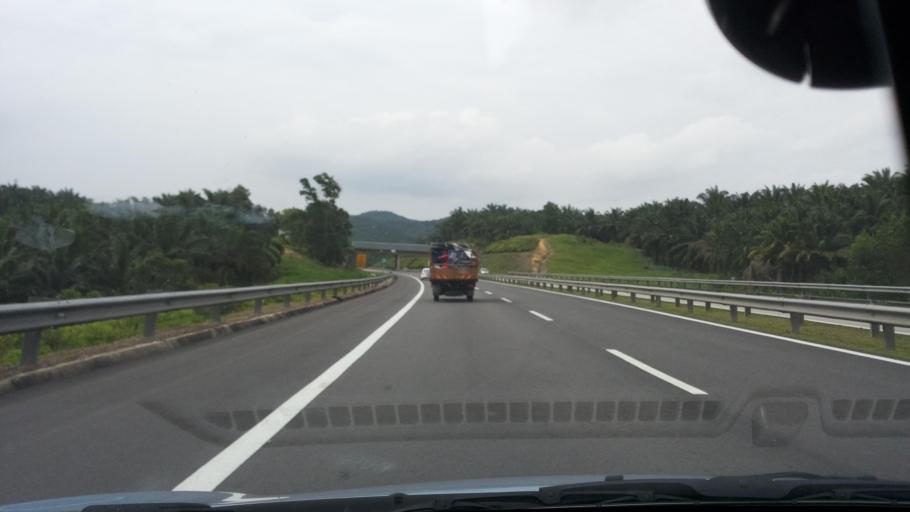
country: MY
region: Pahang
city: Kuantan
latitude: 3.7999
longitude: 103.1619
